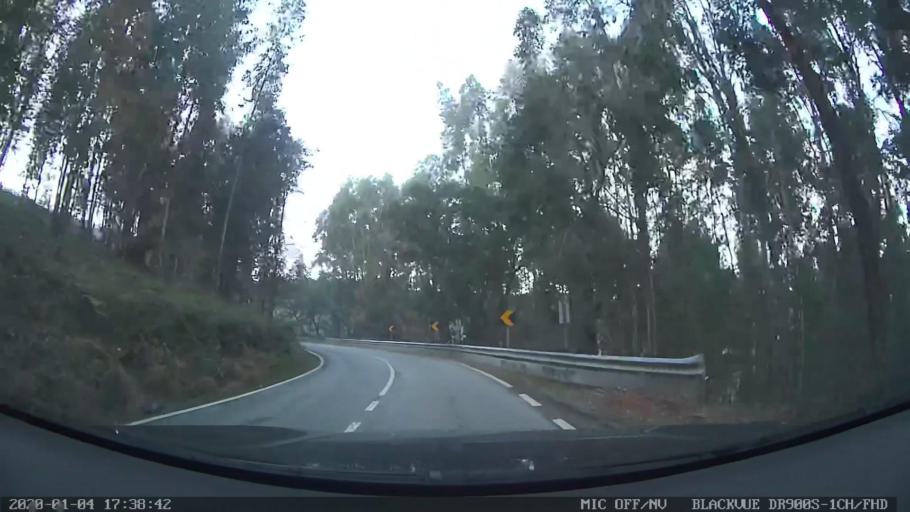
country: PT
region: Vila Real
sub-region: Mondim de Basto
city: Mondim de Basto
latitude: 41.4566
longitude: -7.9601
